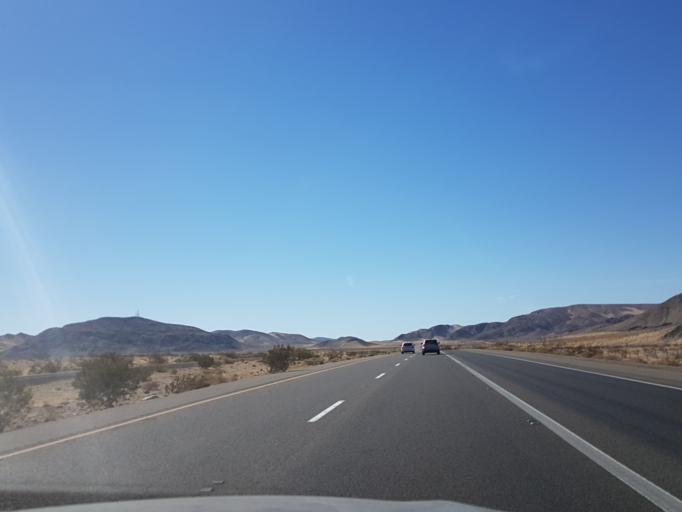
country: US
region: California
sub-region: San Bernardino County
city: Fort Irwin
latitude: 35.0880
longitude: -116.3407
